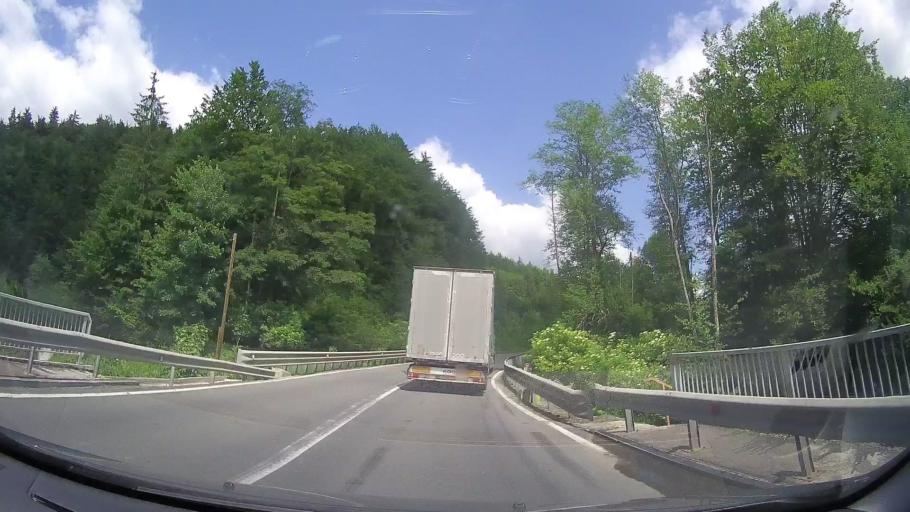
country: RO
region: Prahova
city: Maneciu
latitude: 45.3643
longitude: 25.9311
